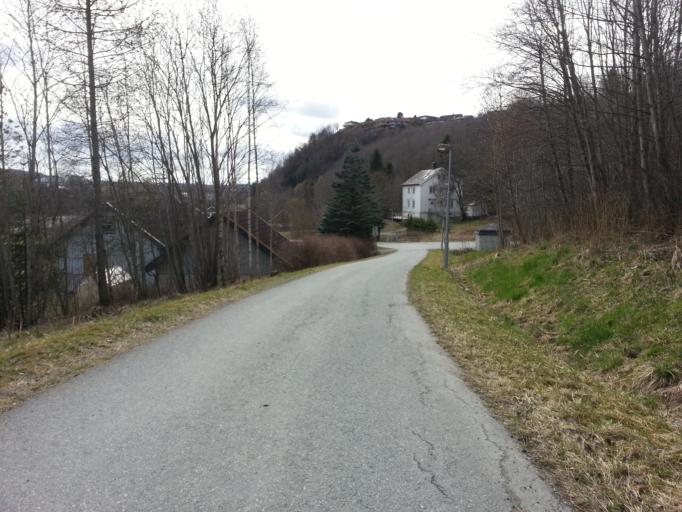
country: NO
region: Sor-Trondelag
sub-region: Trondheim
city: Trondheim
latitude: 63.4077
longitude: 10.3860
